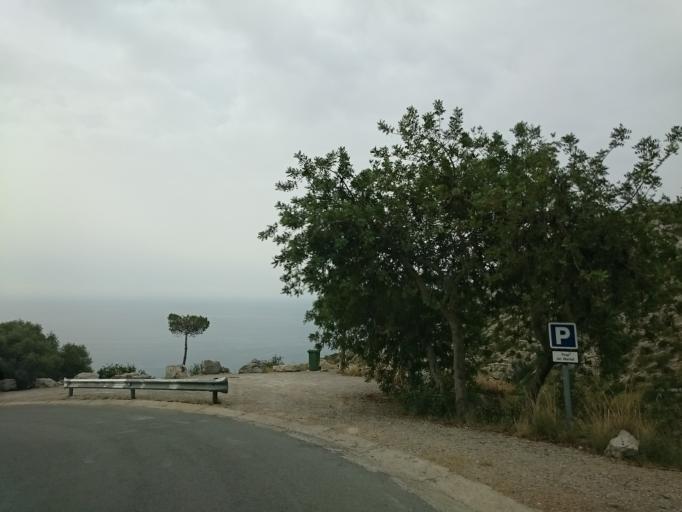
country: ES
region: Catalonia
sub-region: Provincia de Barcelona
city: Castelldefels
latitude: 41.2715
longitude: 1.9192
